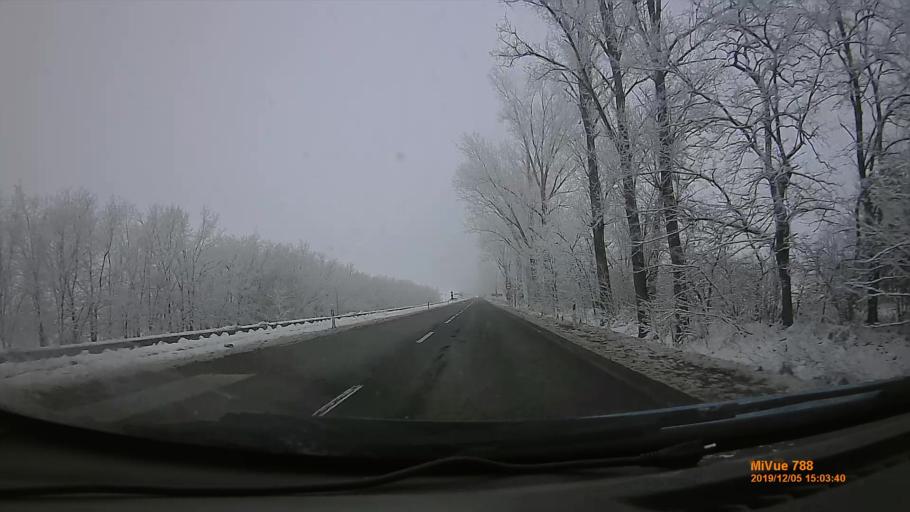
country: HU
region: Szabolcs-Szatmar-Bereg
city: Tiszanagyfalu
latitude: 48.0866
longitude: 21.4976
